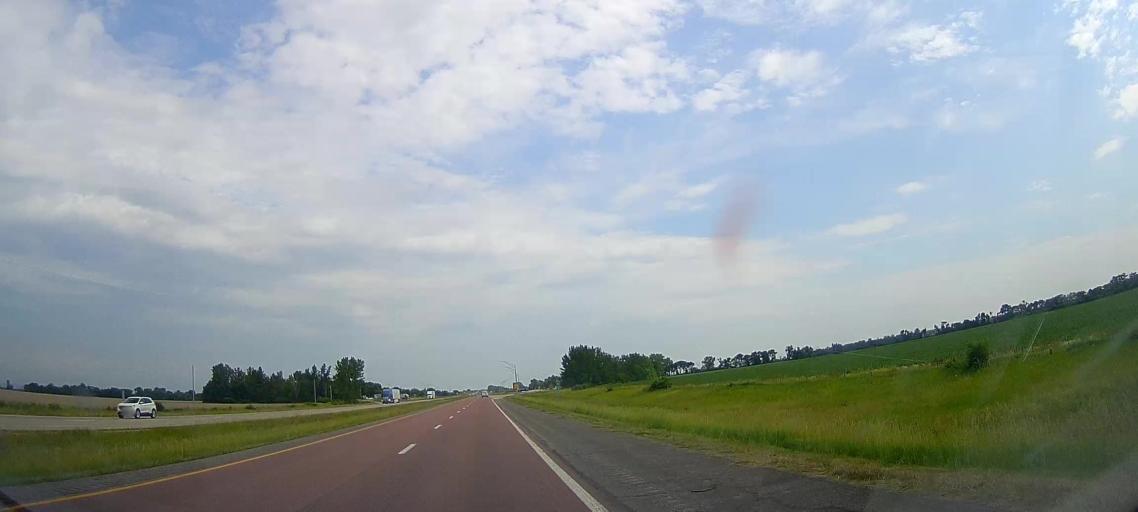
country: US
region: Iowa
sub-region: Monona County
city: Onawa
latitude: 41.9976
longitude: -96.1129
